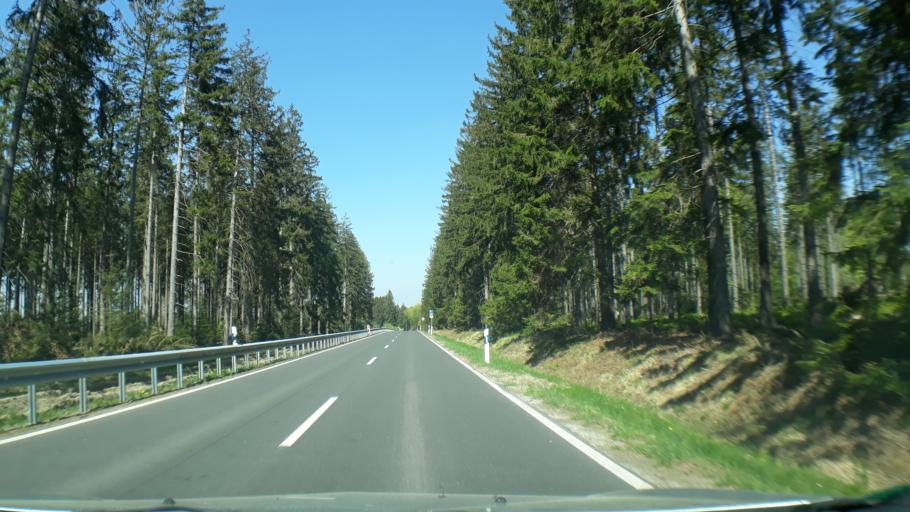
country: DE
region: North Rhine-Westphalia
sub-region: Regierungsbezirk Koln
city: Roetgen
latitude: 50.6647
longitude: 6.2468
